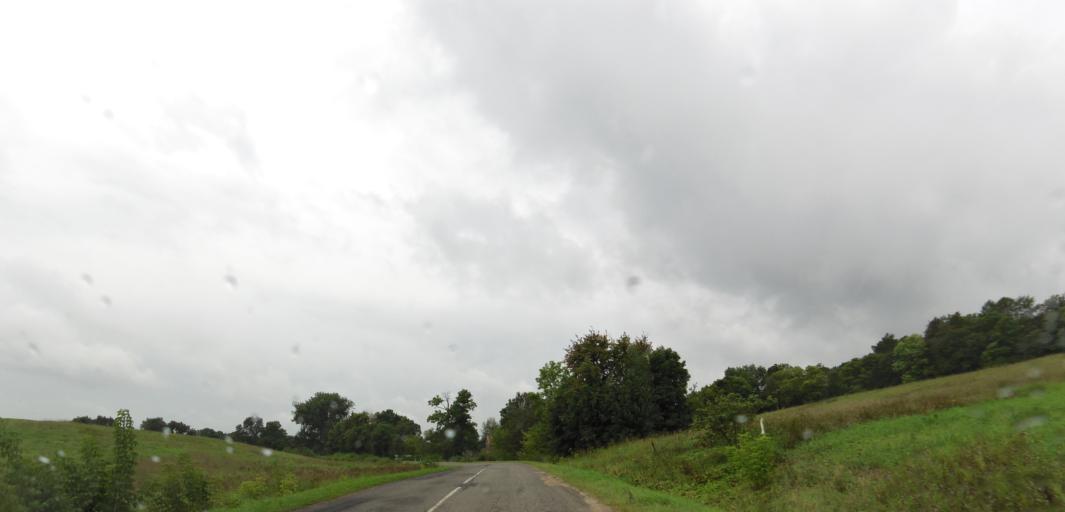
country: LT
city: Sirvintos
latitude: 55.0776
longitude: 25.0680
